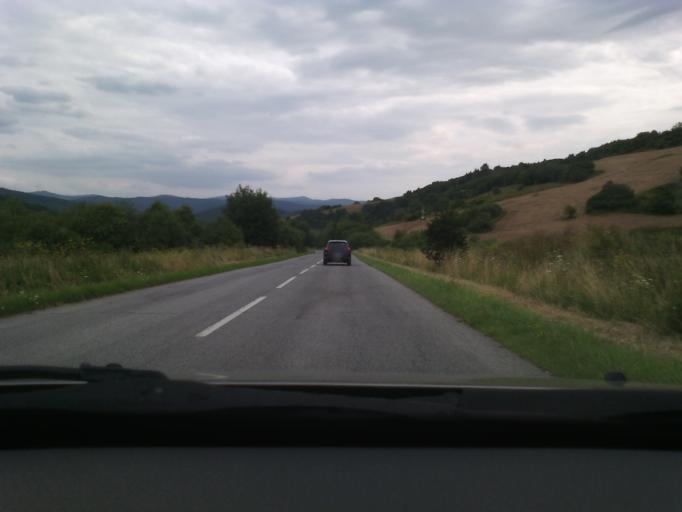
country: SK
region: Presovsky
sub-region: Okres Stara Lubovna
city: Vysne Ruzbachy
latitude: 49.2977
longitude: 20.5650
